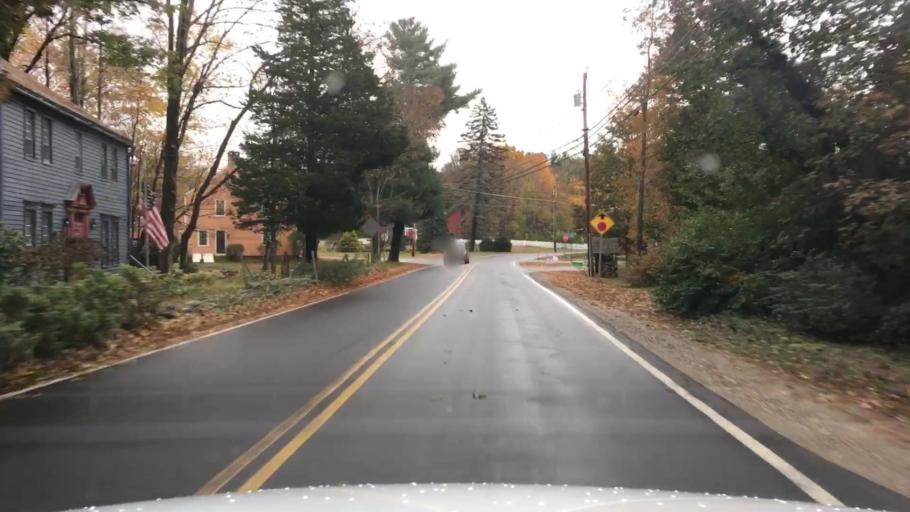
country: US
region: New Hampshire
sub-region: Strafford County
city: Lee
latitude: 43.1226
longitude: -71.0134
